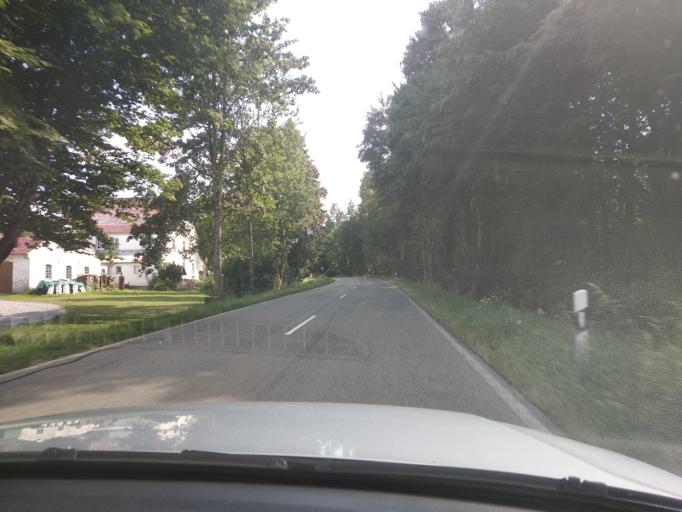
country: DE
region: Baden-Wuerttemberg
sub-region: Tuebingen Region
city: Leutkirch im Allgau
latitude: 47.8703
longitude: 9.9941
